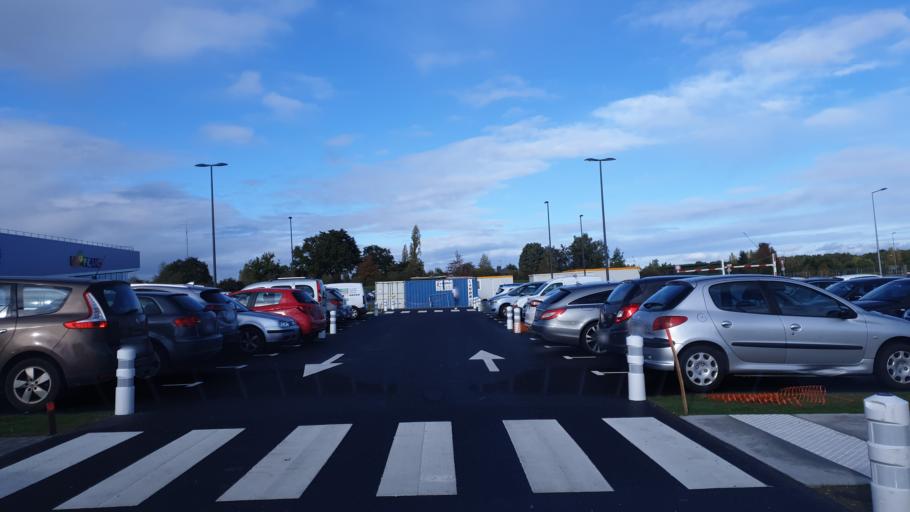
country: FR
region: Brittany
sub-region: Departement d'Ille-et-Vilaine
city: Chantepie
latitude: 48.0652
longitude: -1.6260
